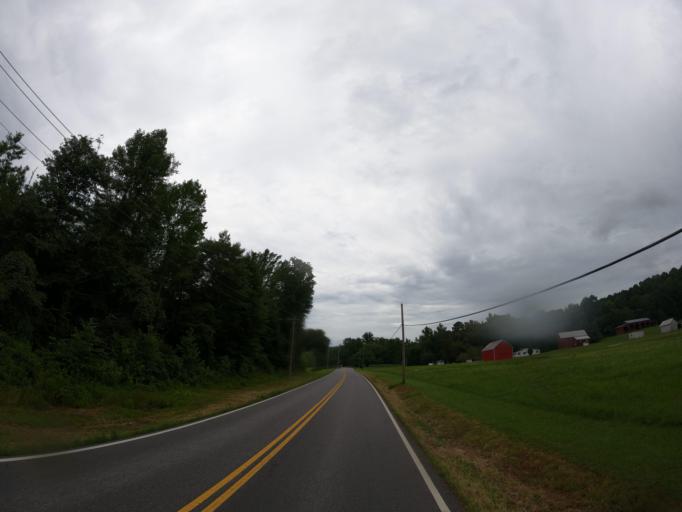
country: US
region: Maryland
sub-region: Saint Mary's County
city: California
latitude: 38.2492
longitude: -76.5064
